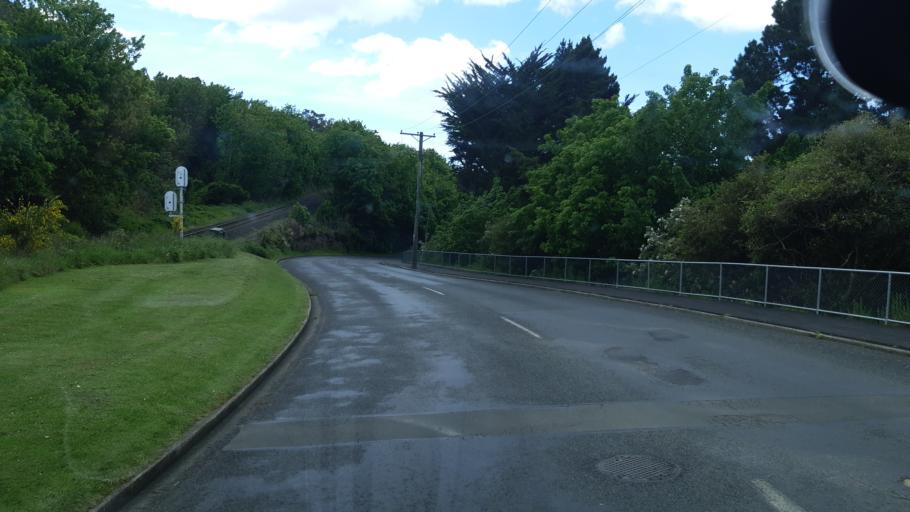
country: NZ
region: Otago
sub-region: Dunedin City
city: Portobello
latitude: -45.8182
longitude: 170.6153
